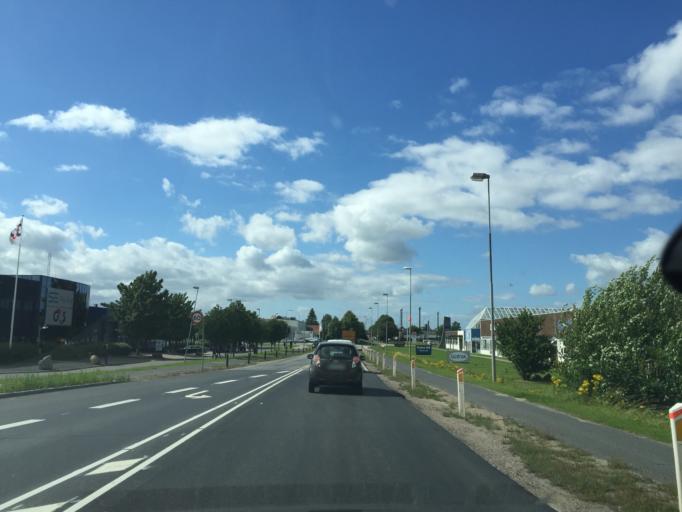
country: DK
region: South Denmark
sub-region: Odense Kommune
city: Hojby
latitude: 55.3526
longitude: 10.4067
